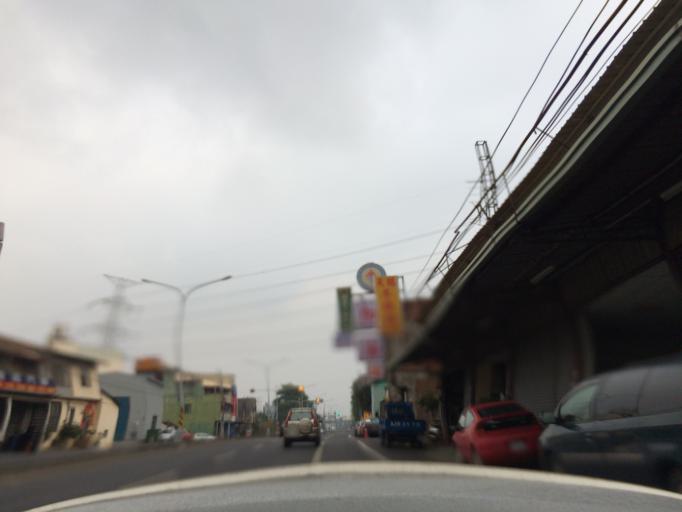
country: TW
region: Taiwan
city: Zhongxing New Village
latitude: 24.0209
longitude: 120.6962
